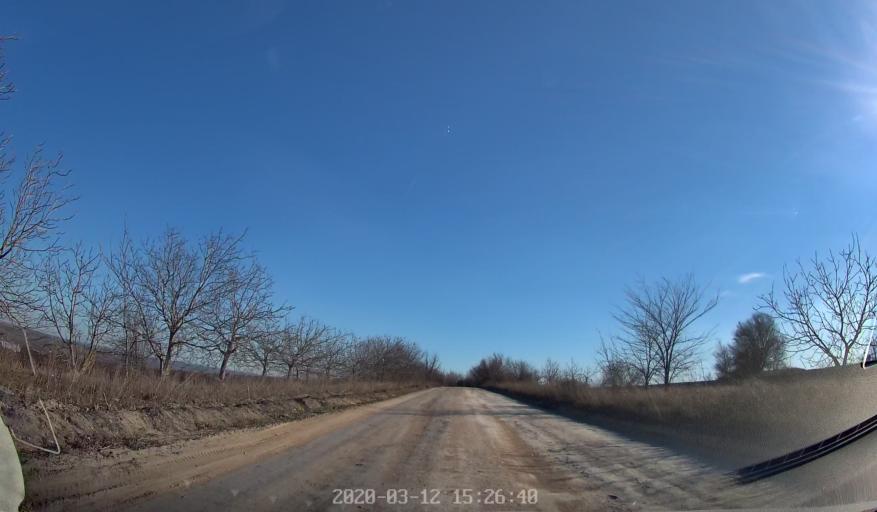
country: MD
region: Chisinau
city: Ciorescu
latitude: 47.1768
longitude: 28.9236
